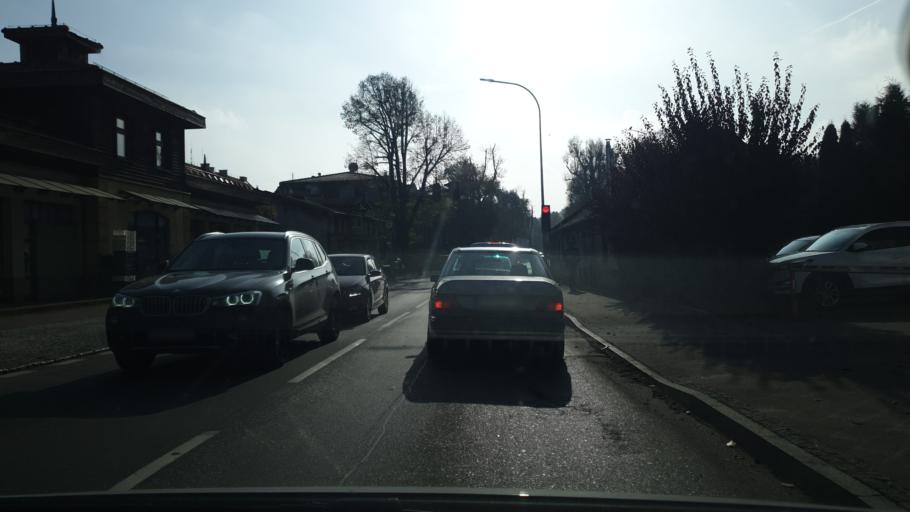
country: PL
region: Pomeranian Voivodeship
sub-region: Sopot
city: Sopot
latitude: 54.4084
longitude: 18.5591
